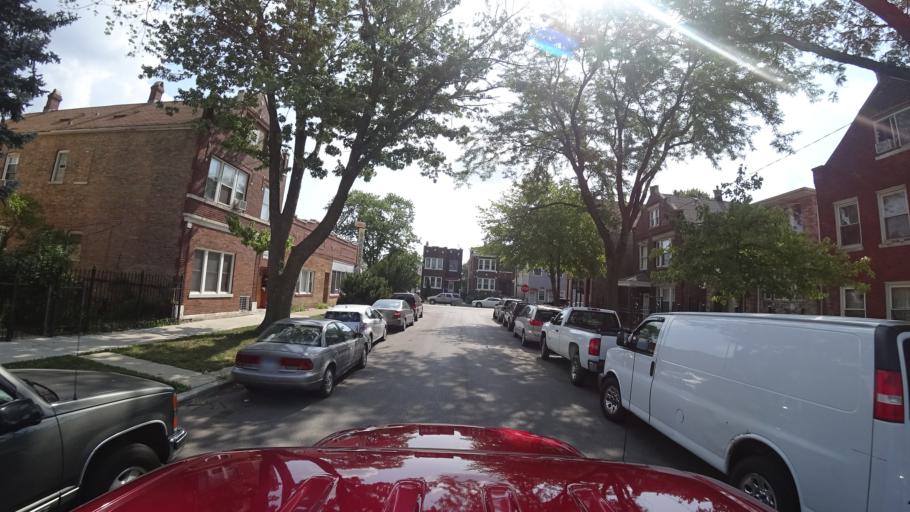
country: US
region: Illinois
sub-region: Cook County
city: Chicago
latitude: 41.8191
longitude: -87.7001
